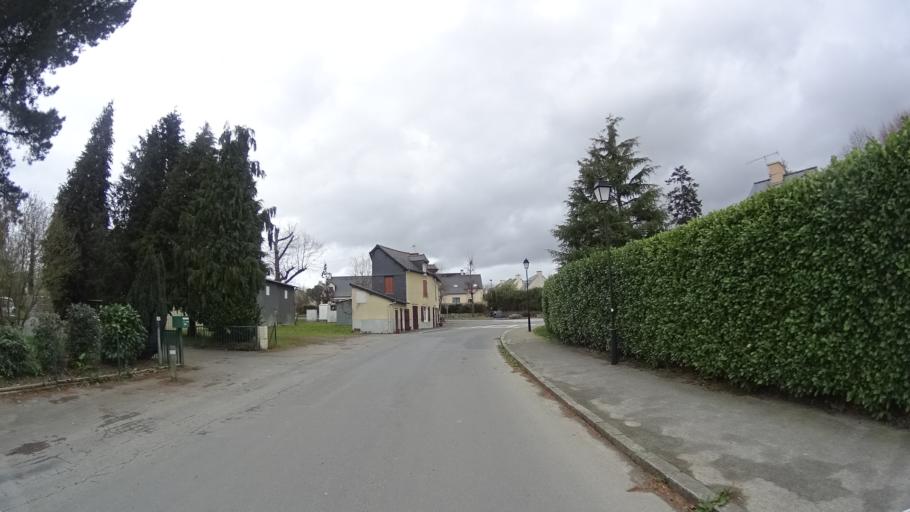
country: FR
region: Brittany
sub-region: Departement d'Ille-et-Vilaine
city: Saint-Gilles
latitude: 48.1913
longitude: -1.8322
